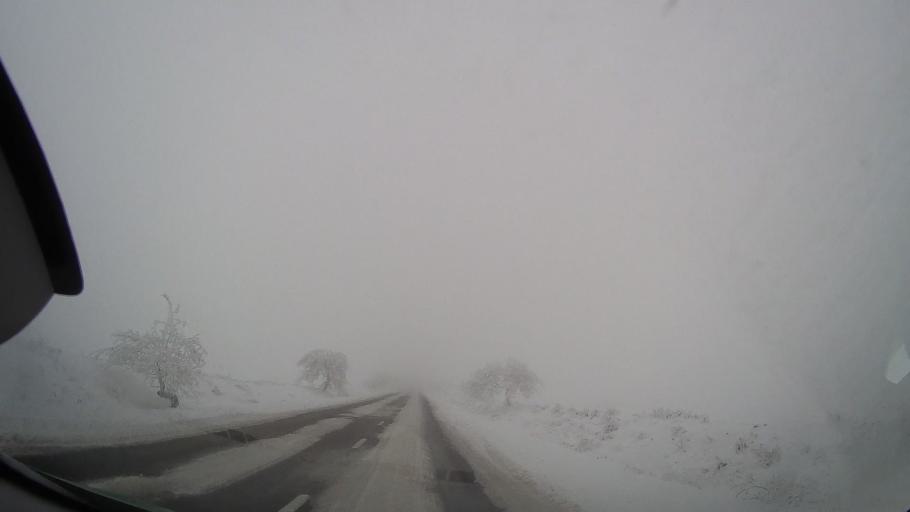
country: RO
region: Neamt
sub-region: Comuna Valea Ursului
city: Valea Ursului
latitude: 46.8201
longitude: 27.0642
